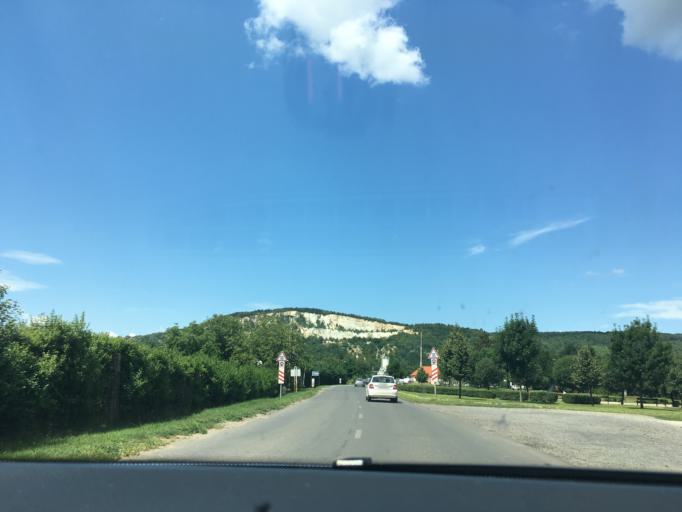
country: HU
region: Borsod-Abauj-Zemplen
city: Tarcal
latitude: 48.1725
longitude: 21.3535
